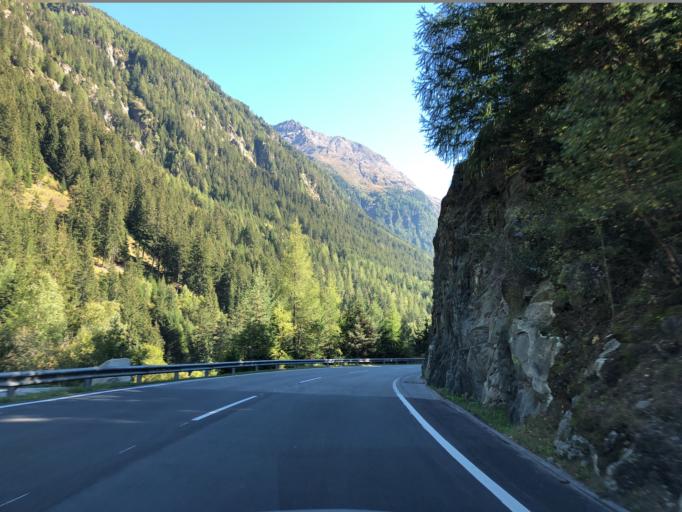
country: AT
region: Tyrol
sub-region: Politischer Bezirk Imst
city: Soelden
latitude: 47.0052
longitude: 11.0084
